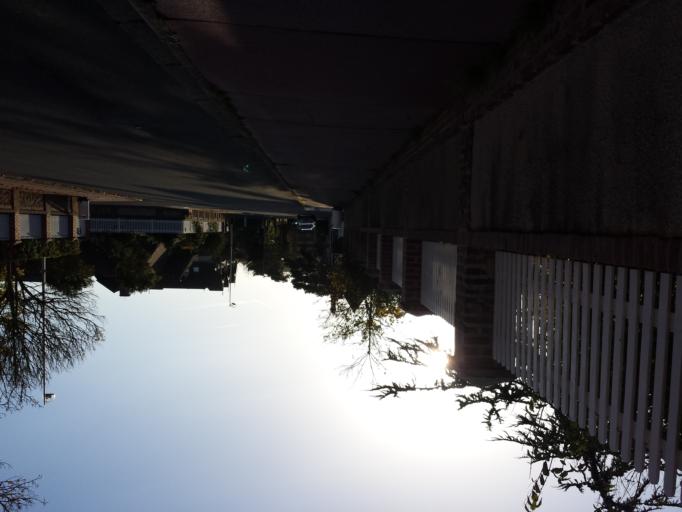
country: FR
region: Lower Normandy
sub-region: Departement du Calvados
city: Deauville
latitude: 49.3552
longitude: 0.0617
